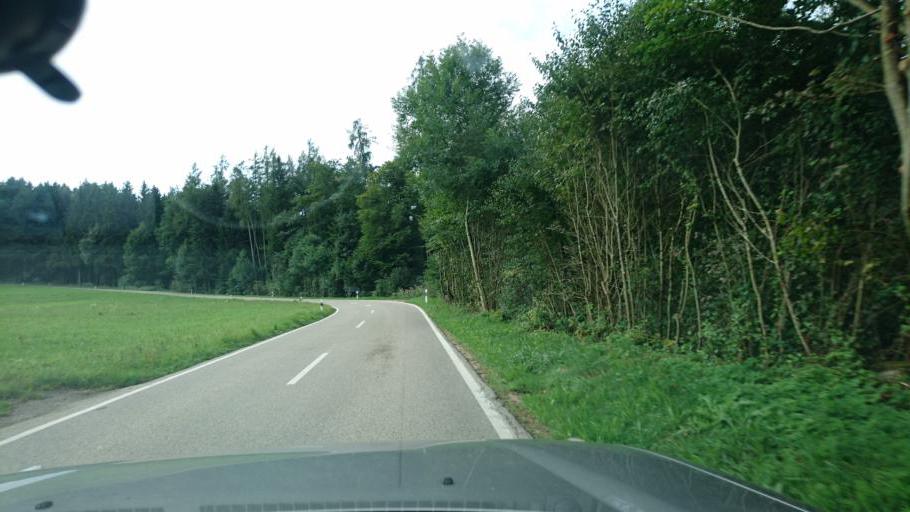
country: DE
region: Bavaria
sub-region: Upper Bavaria
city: Grabenstatt
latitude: 47.8370
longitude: 12.5578
